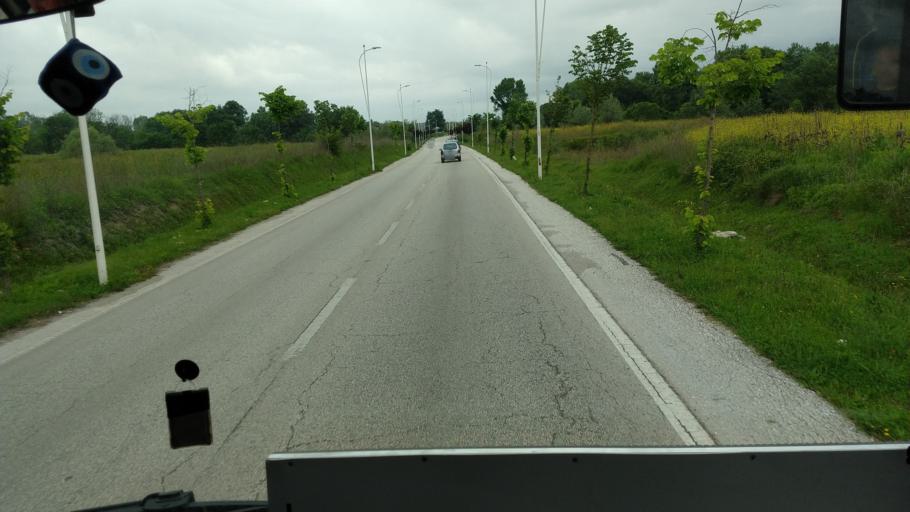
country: AL
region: Tirane
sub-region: Rrethi i Tiranes
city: Berxull
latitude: 41.4108
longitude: 19.7034
